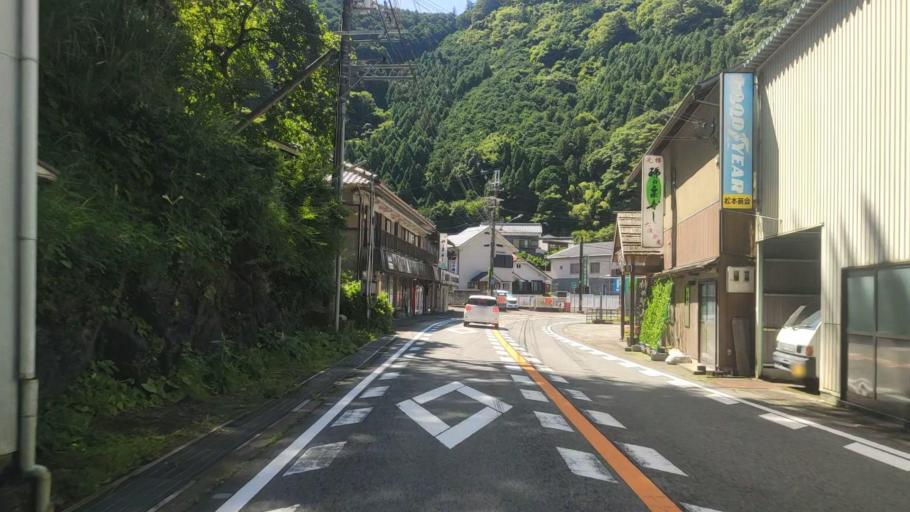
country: JP
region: Nara
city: Yoshino-cho
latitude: 34.3558
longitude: 135.9240
